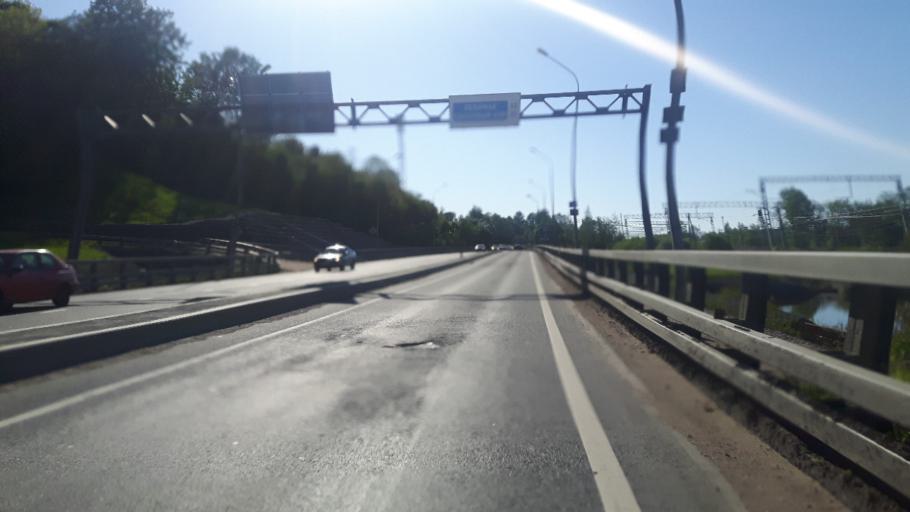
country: RU
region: St.-Petersburg
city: Bol'shaya Izhora
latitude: 59.9265
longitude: 29.6655
